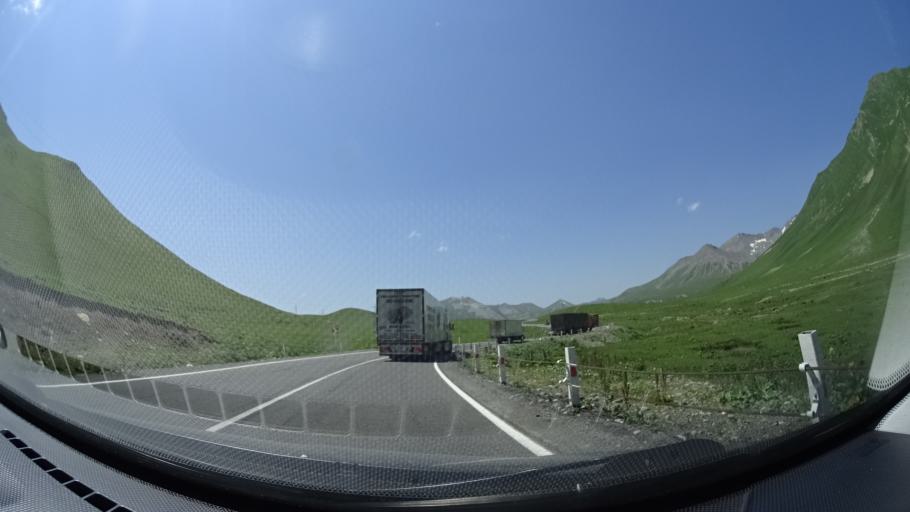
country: GE
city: Gudauri
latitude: 42.5103
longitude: 44.4619
